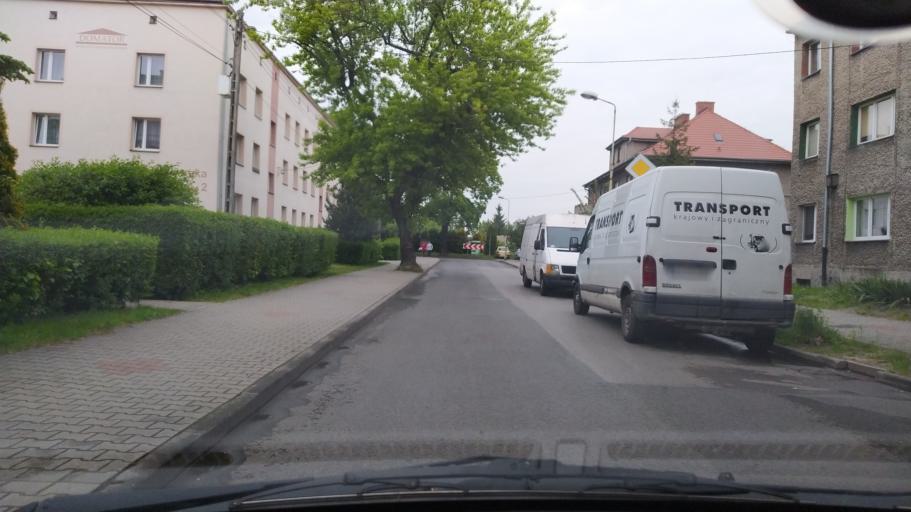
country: PL
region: Silesian Voivodeship
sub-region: Powiat gliwicki
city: Przyszowice
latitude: 50.2921
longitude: 18.7401
